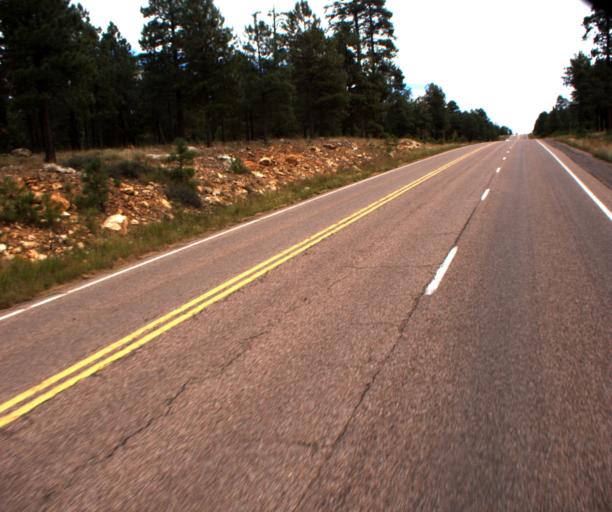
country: US
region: Arizona
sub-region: Navajo County
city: Heber-Overgaard
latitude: 34.3320
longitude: -110.7617
